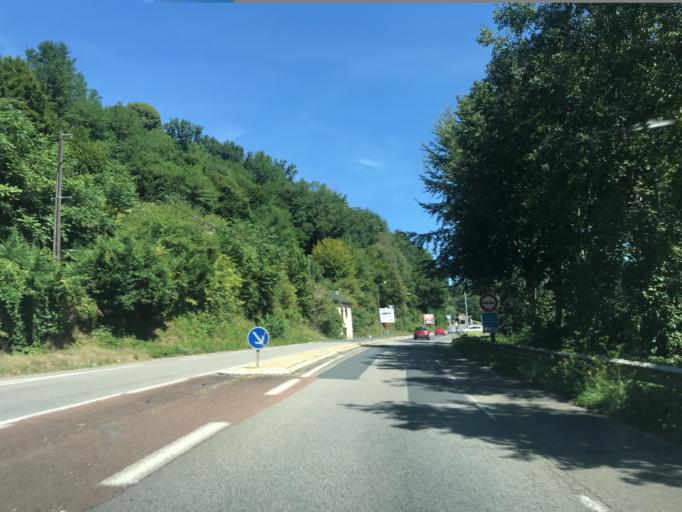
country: FR
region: Limousin
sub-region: Departement de la Correze
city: Tulle
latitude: 45.2479
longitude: 1.7470
